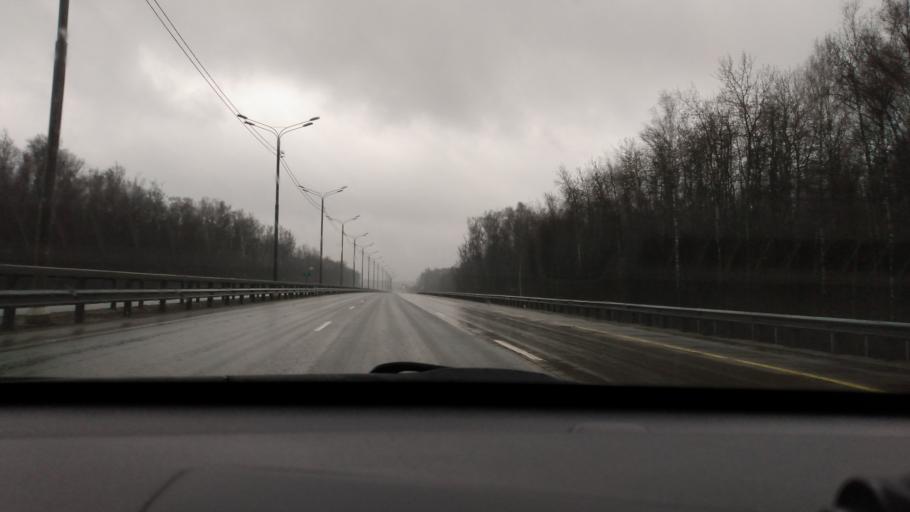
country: RU
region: Moskovskaya
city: Barybino
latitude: 55.2043
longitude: 37.8858
